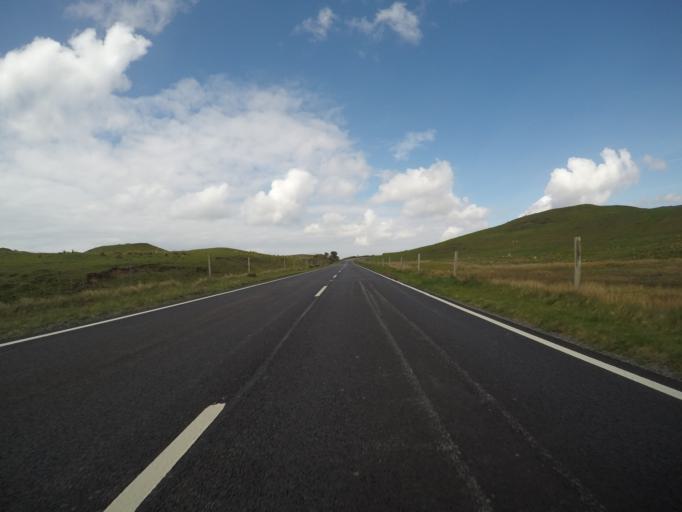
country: GB
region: Scotland
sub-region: Highland
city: Portree
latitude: 57.5437
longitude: -6.3651
